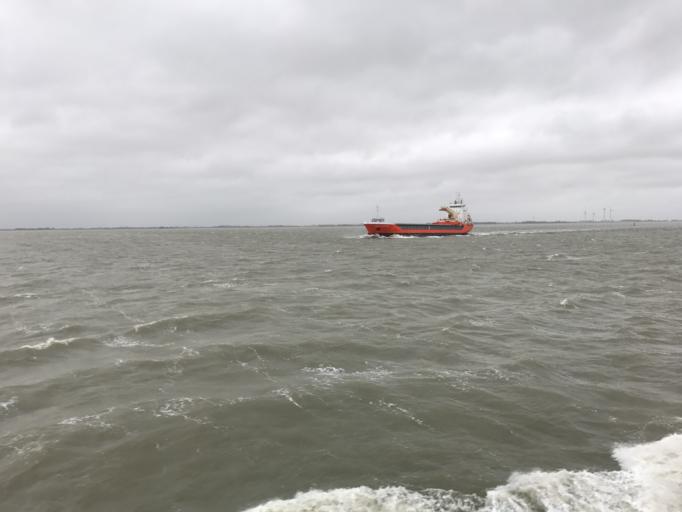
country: NL
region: Groningen
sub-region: Gemeente Delfzijl
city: Delfzijl
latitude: 53.3938
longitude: 6.9545
